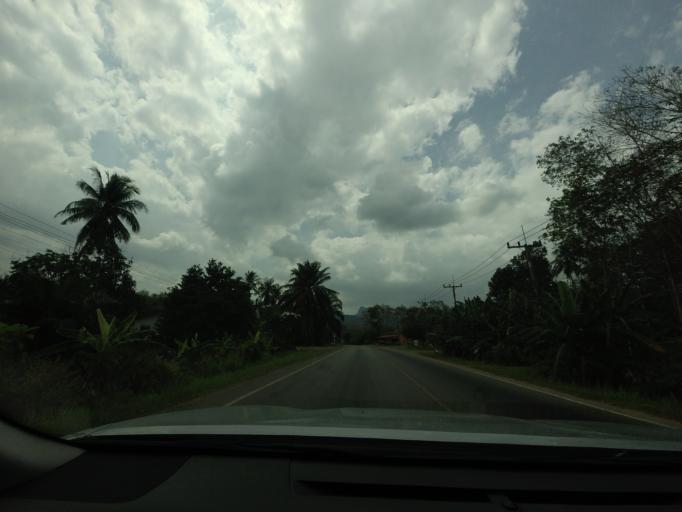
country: TH
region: Phangnga
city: Ban Ao Nang
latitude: 8.1203
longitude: 98.8022
